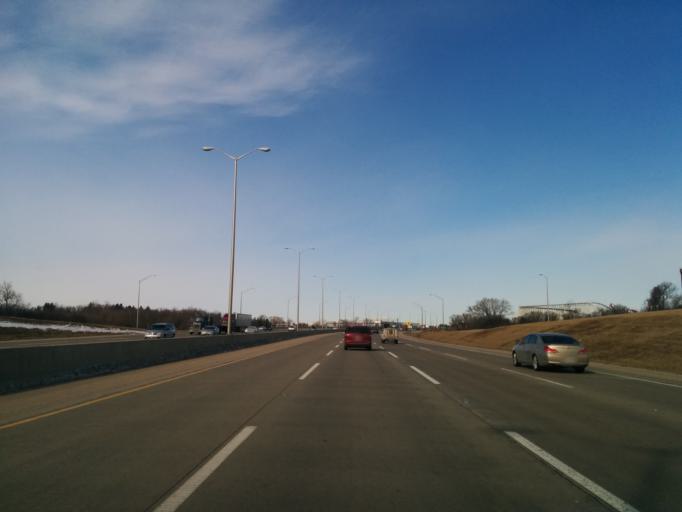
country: US
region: Illinois
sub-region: Lake County
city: Gurnee
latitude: 42.3587
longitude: -87.9354
